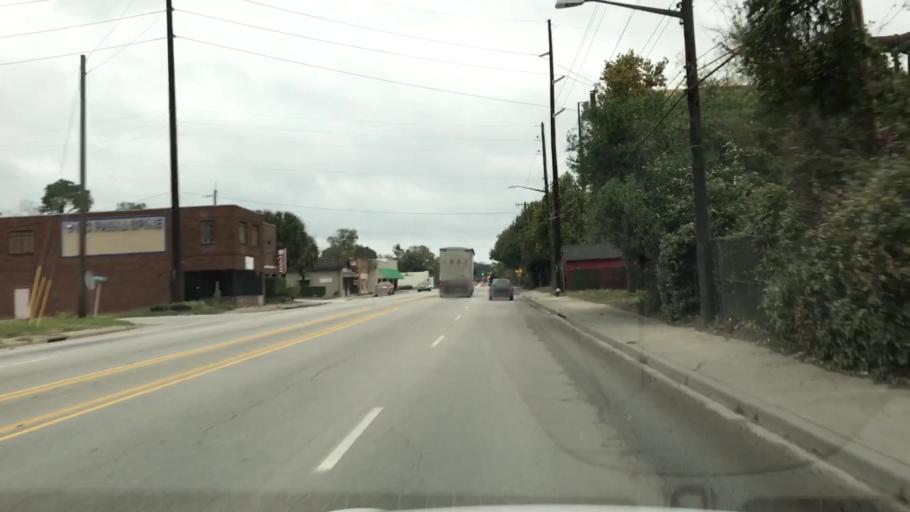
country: US
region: South Carolina
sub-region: Georgetown County
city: Georgetown
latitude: 33.3685
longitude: -79.2925
